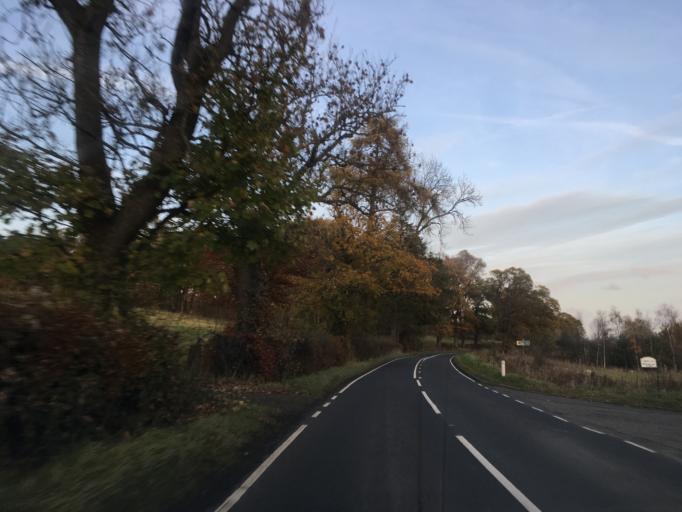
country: GB
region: Scotland
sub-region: Clackmannanshire
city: Dollar
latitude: 56.1650
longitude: -3.6615
